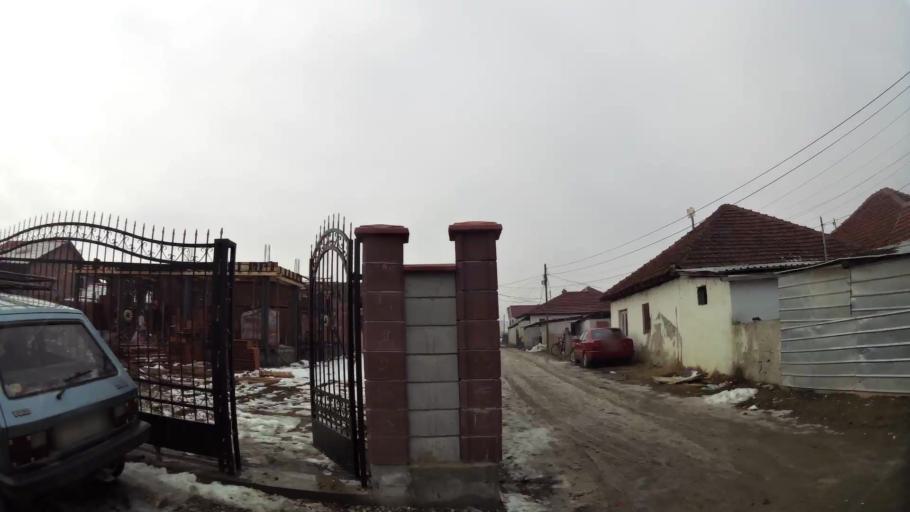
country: MK
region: Ilinden
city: Ilinden
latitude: 41.9921
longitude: 21.5714
